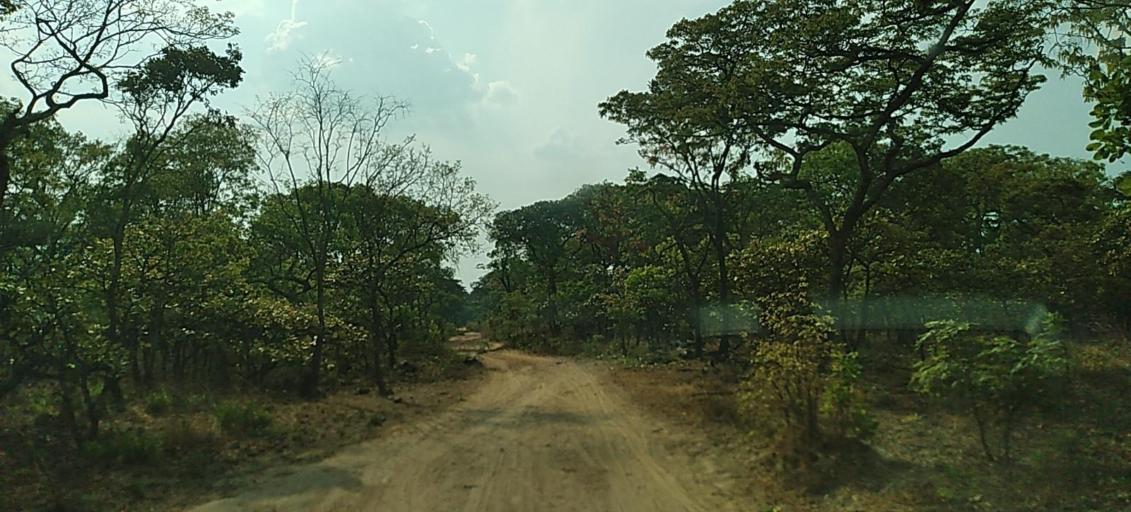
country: ZM
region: North-Western
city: Solwezi
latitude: -12.0721
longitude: 26.2295
